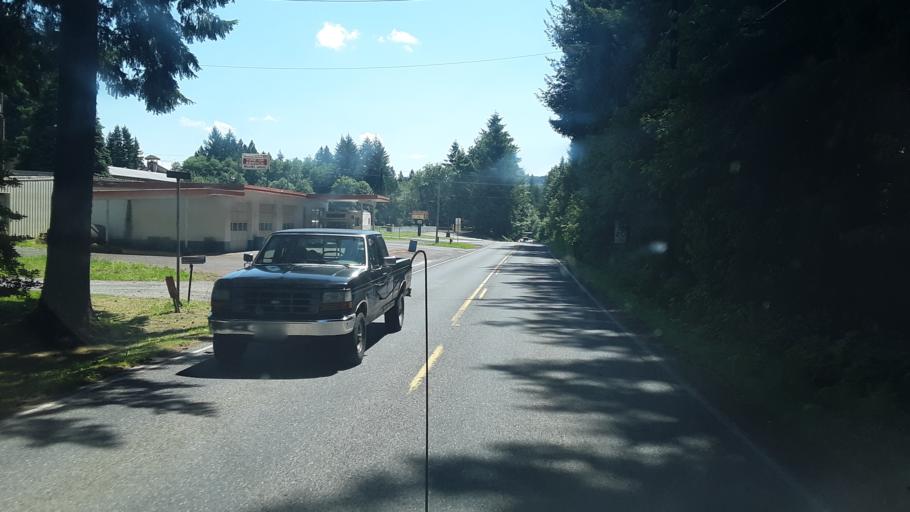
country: US
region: Washington
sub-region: Clark County
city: Amboy
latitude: 45.9148
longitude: -122.4468
